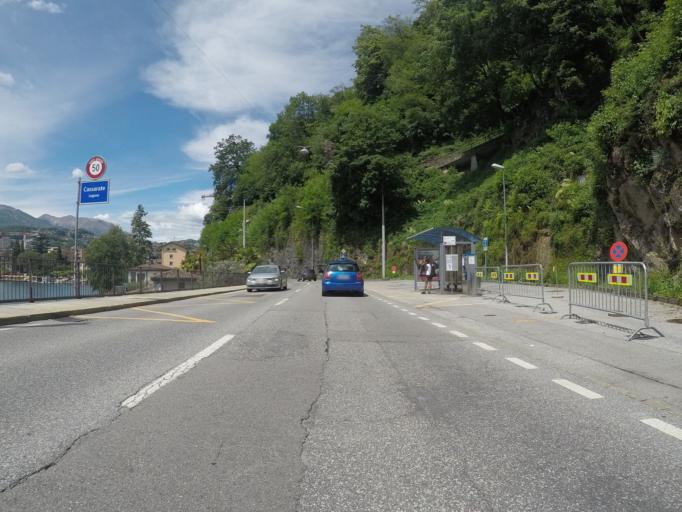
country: CH
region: Ticino
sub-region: Lugano District
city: Viganello
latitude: 46.0033
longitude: 8.9713
